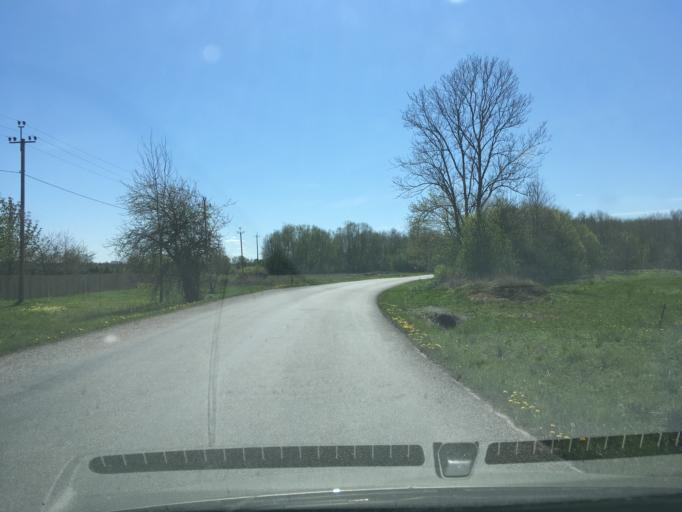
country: EE
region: Harju
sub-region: Raasiku vald
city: Arukula
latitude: 59.4062
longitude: 25.0780
